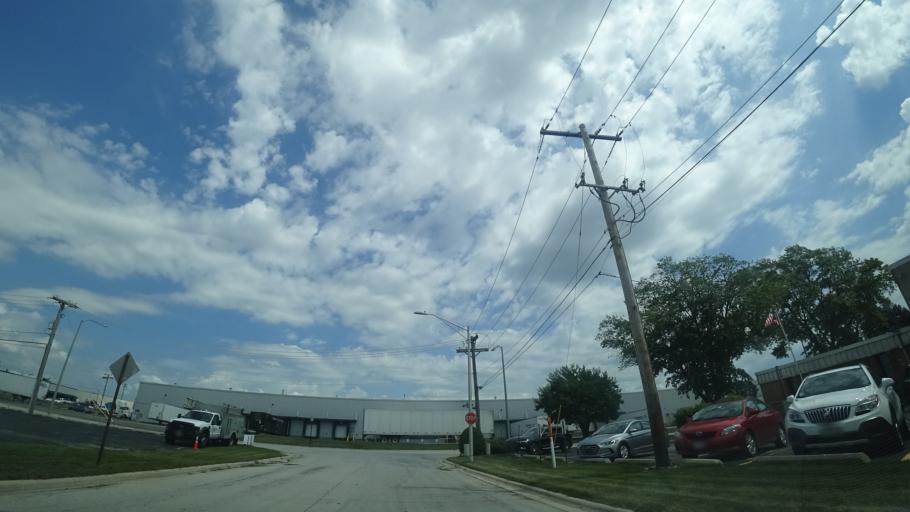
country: US
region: Illinois
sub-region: Cook County
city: Crestwood
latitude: 41.6681
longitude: -87.7492
